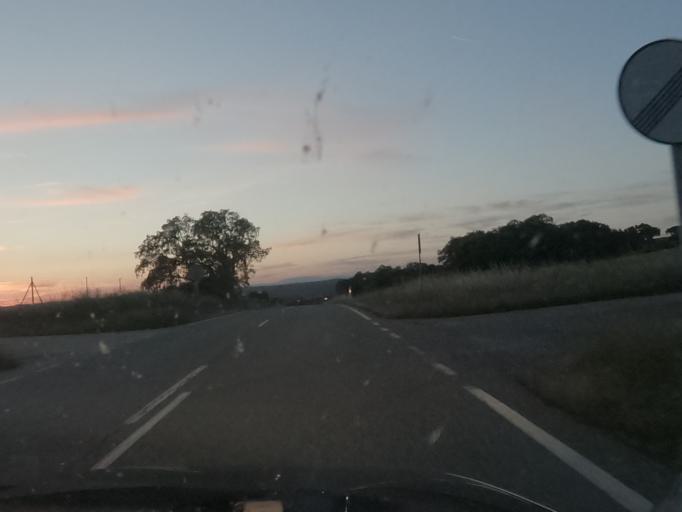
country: ES
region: Extremadura
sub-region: Provincia de Caceres
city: Piedras Albas
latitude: 39.7935
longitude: -6.9597
